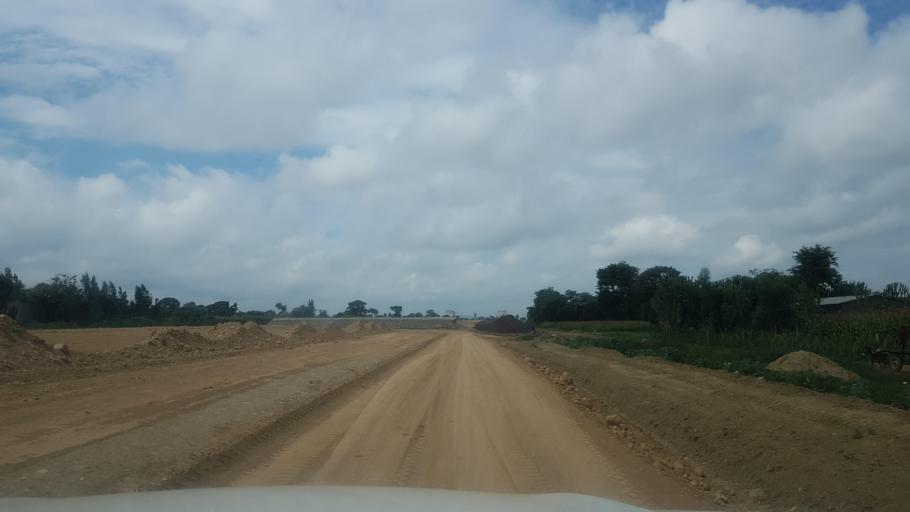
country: ET
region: Oromiya
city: Shashemene
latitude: 7.2616
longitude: 38.5958
